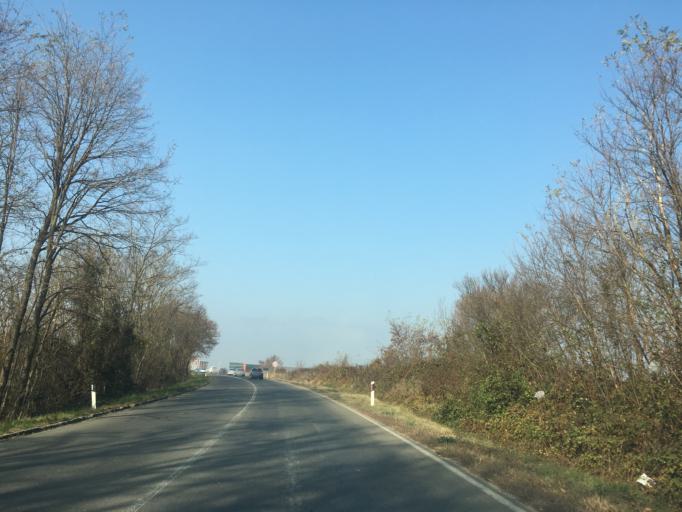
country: XK
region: Pec
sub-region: Komuna e Pejes
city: Dubova (Driloni)
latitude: 42.6475
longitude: 20.4106
